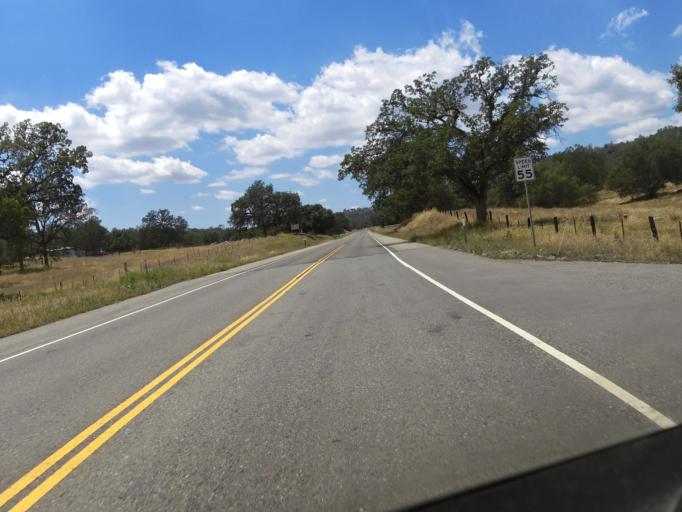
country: US
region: California
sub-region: Madera County
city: Coarsegold
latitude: 37.1532
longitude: -119.6535
